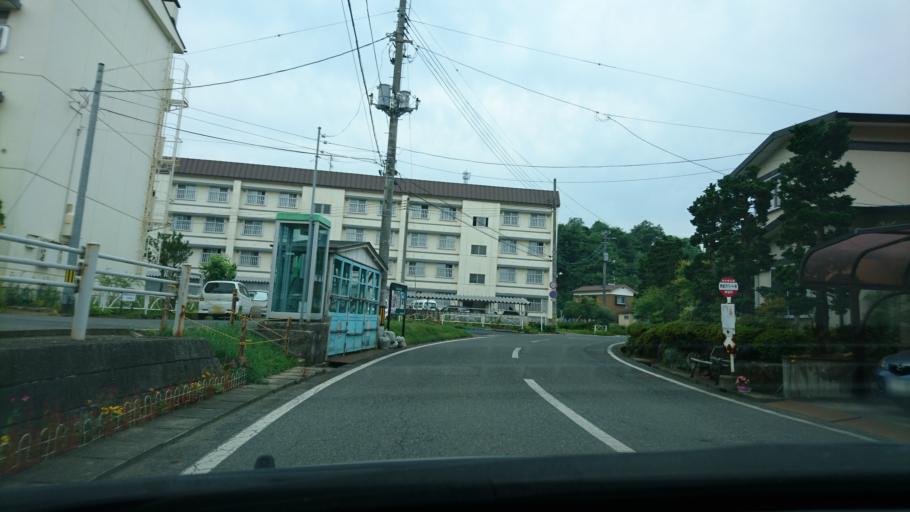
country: JP
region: Iwate
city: Ichinoseki
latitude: 38.9147
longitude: 141.1489
